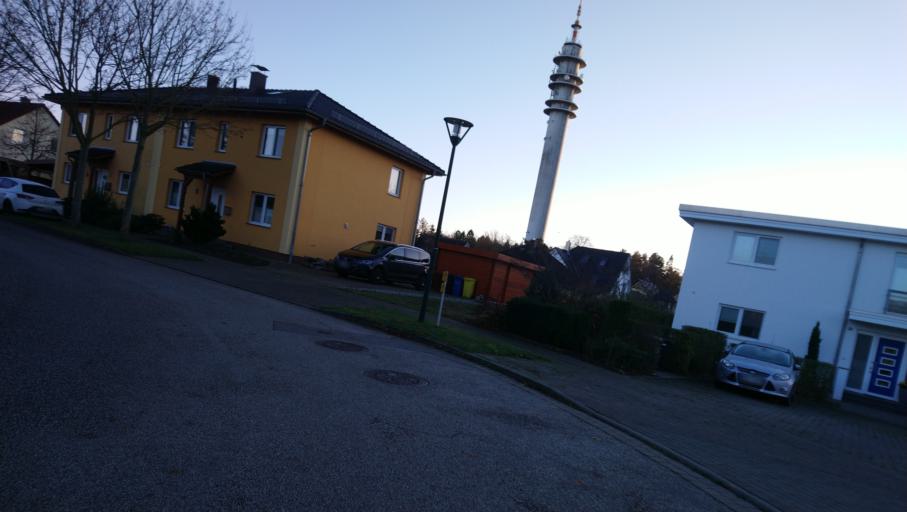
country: DE
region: Mecklenburg-Vorpommern
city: Kritzmow
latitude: 54.0737
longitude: 12.0784
